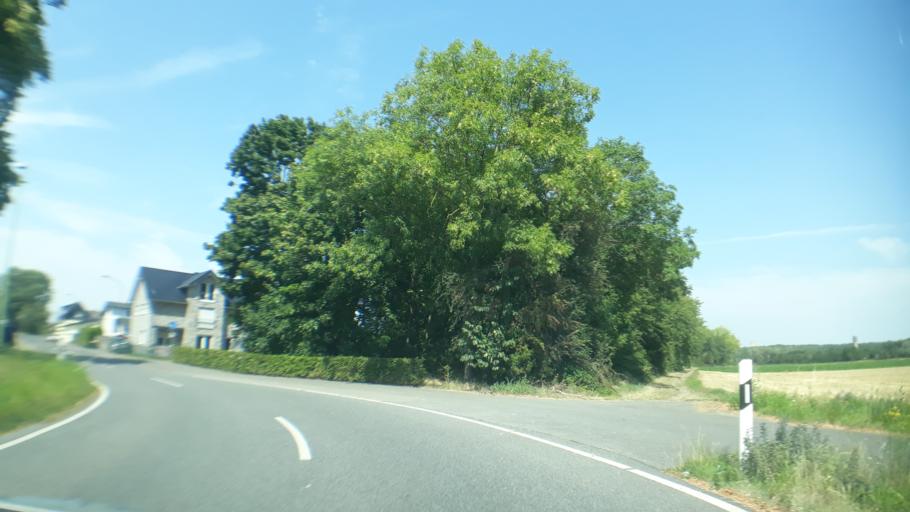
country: DE
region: North Rhine-Westphalia
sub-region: Regierungsbezirk Koln
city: Langerwehe
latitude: 50.8363
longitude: 6.3461
